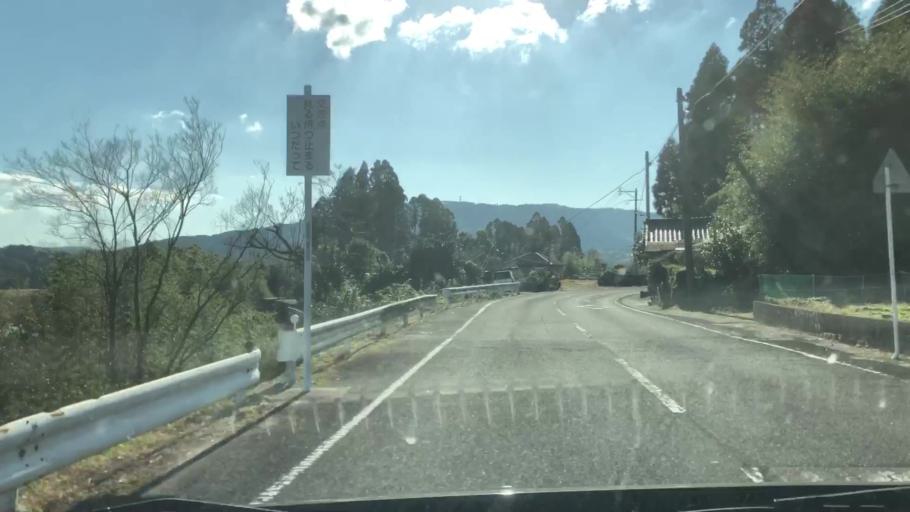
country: JP
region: Kagoshima
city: Satsumasendai
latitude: 31.8555
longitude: 130.3630
